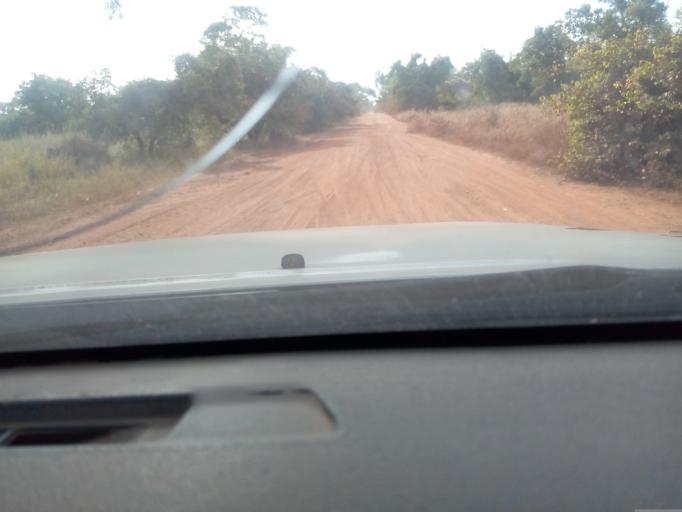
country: ML
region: Sikasso
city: Sikasso
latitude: 11.9340
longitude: -6.0750
